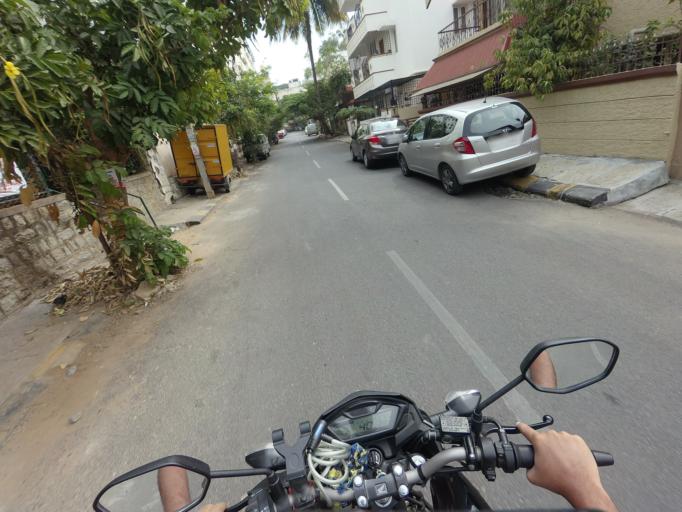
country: IN
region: Karnataka
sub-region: Bangalore Urban
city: Bangalore
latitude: 12.9701
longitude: 77.5355
